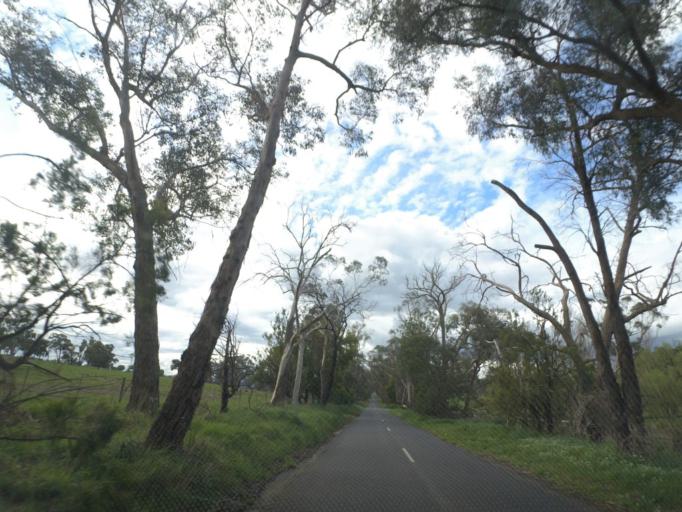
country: AU
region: Victoria
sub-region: Yarra Ranges
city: Mount Evelyn
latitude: -37.7447
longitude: 145.4122
